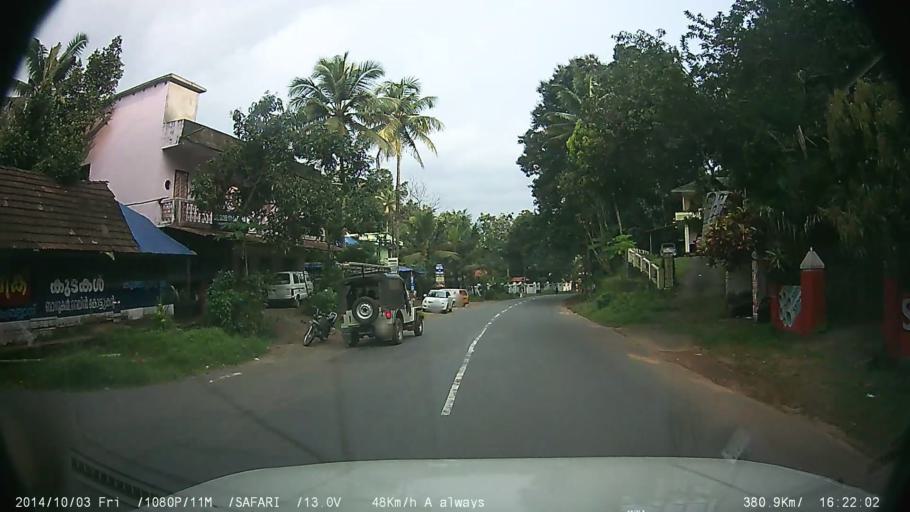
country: IN
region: Kerala
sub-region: Ernakulam
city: Piravam
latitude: 9.8820
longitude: 76.5945
